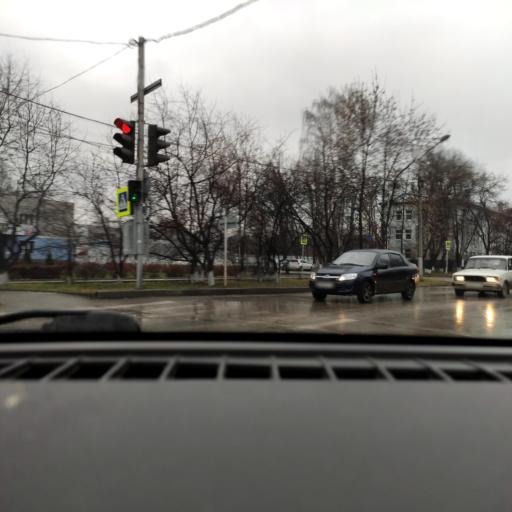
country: RU
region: Perm
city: Kultayevo
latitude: 57.9918
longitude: 55.9340
